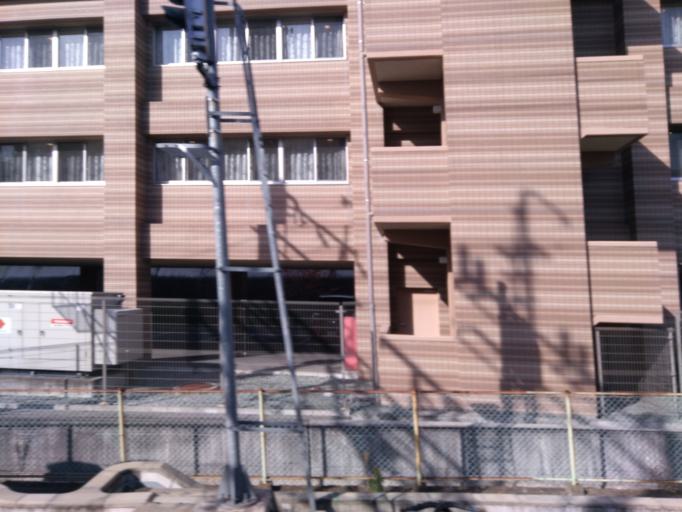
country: JP
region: Hyogo
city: Takarazuka
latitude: 34.8167
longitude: 135.3625
